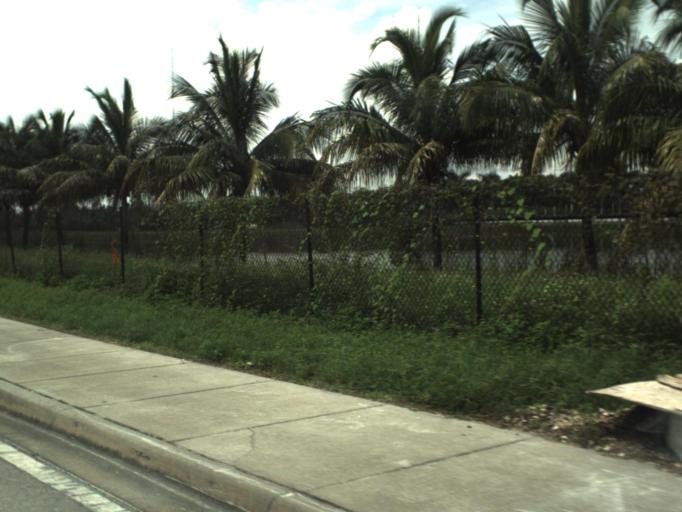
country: US
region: Florida
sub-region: Miami-Dade County
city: Tamiami
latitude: 25.7801
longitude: -80.4173
